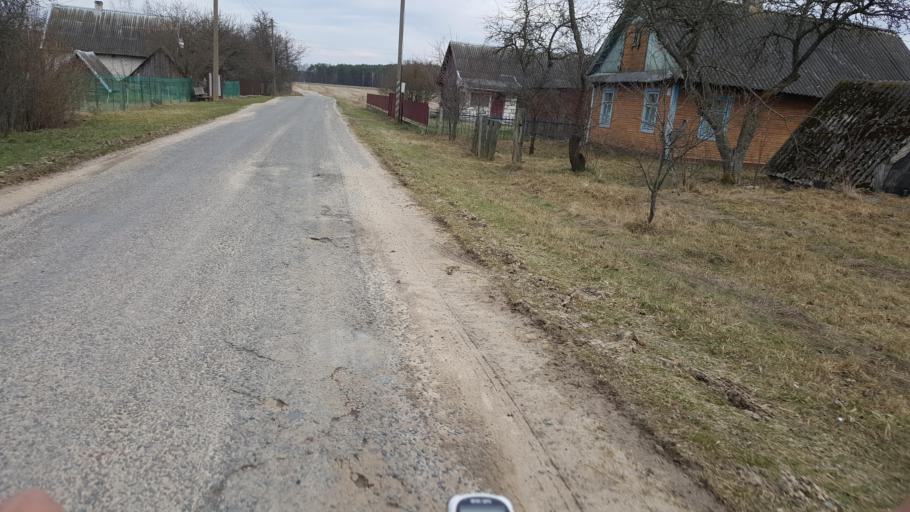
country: BY
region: Brest
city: Kamyanyets
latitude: 52.3669
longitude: 23.9654
